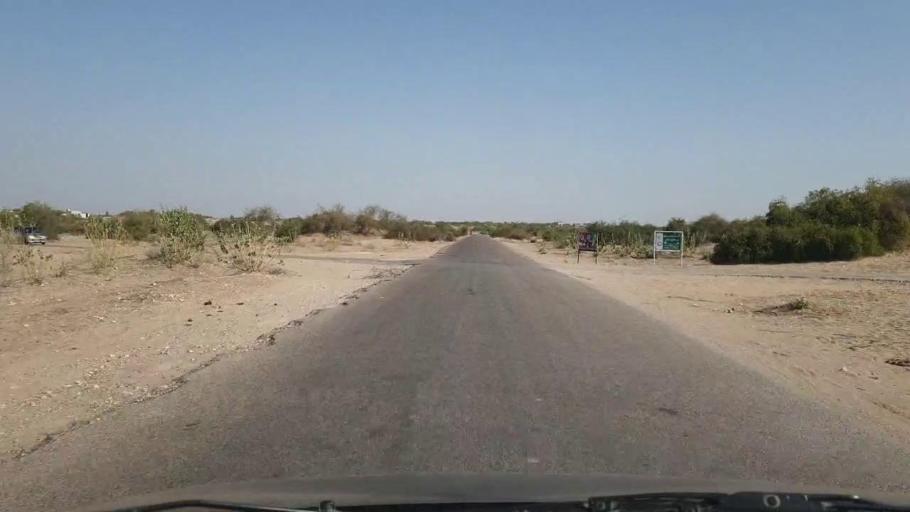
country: PK
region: Sindh
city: Chor
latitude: 25.5075
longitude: 69.8177
